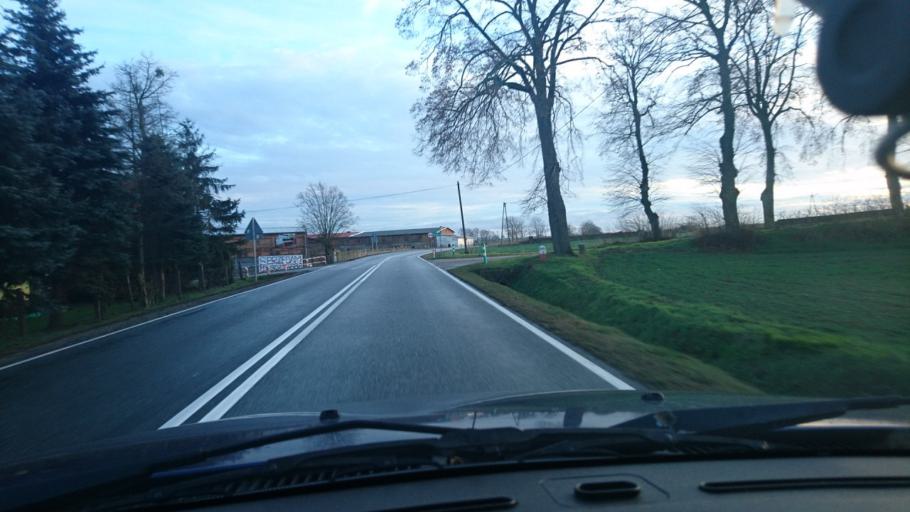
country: PL
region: Opole Voivodeship
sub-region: Powiat kluczborski
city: Byczyna
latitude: 51.1363
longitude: 18.1986
